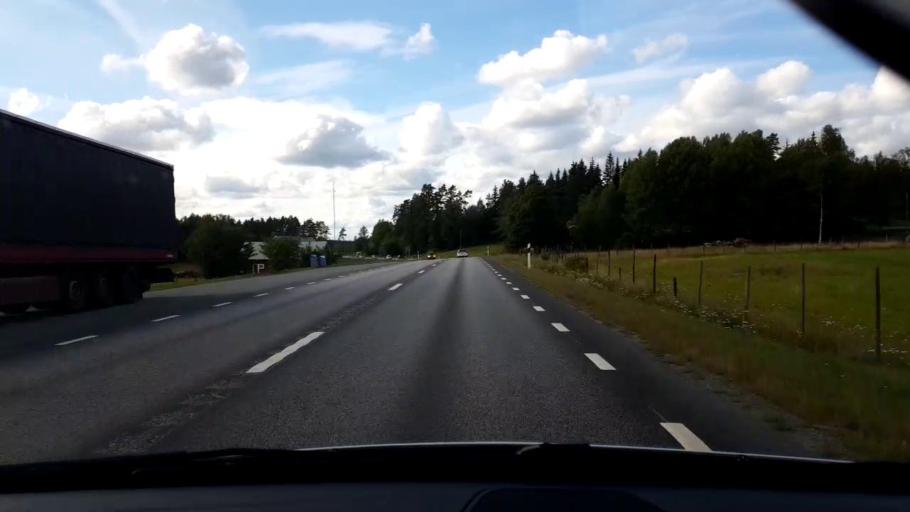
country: SE
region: Joenkoeping
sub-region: Savsjo Kommun
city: Vrigstad
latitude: 57.3631
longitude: 14.4547
